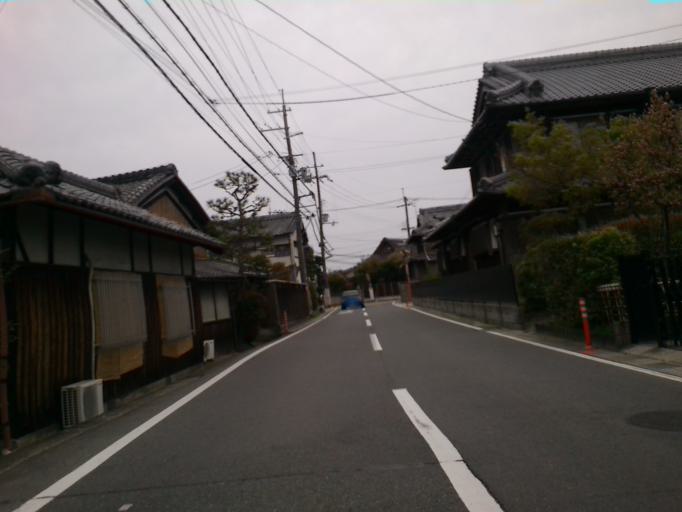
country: JP
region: Kyoto
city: Tanabe
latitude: 34.8375
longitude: 135.7499
